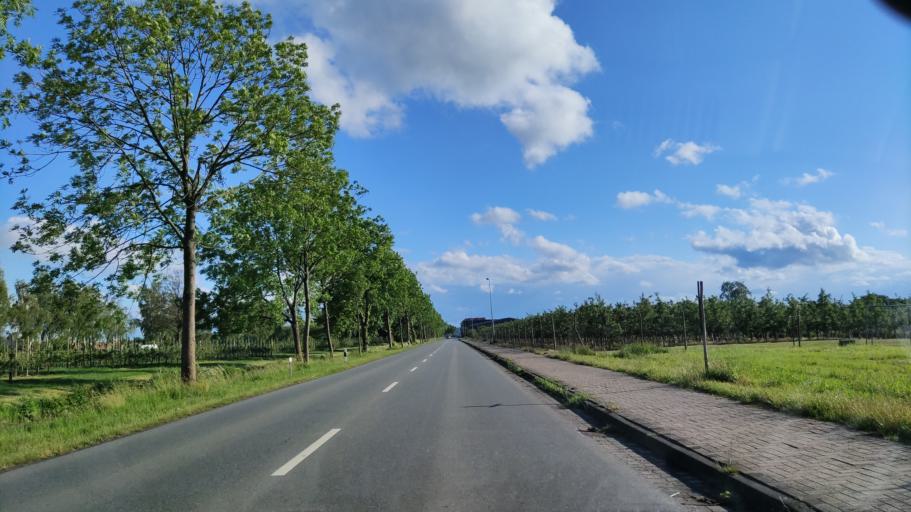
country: DE
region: Lower Saxony
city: Jork
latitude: 53.5221
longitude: 9.6735
